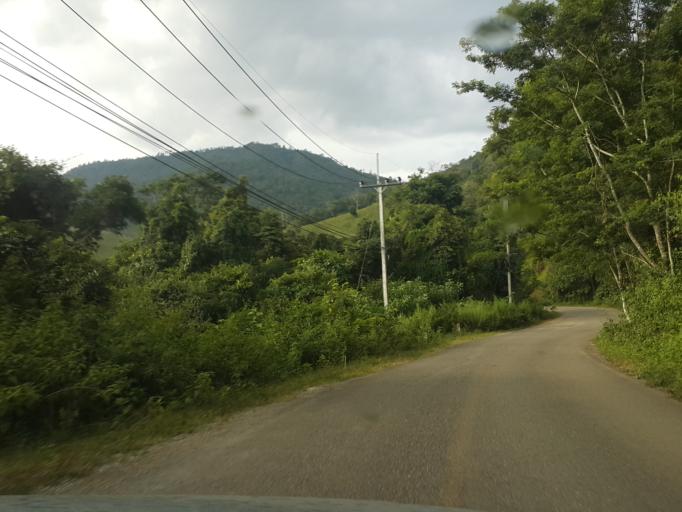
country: TH
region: Mae Hong Son
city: Khun Yuam
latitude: 18.7526
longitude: 98.1923
